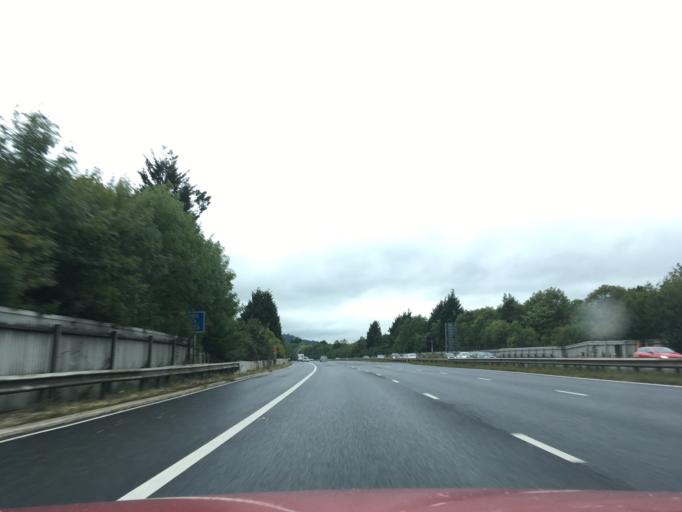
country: GB
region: England
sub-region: Gloucestershire
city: Barnwood
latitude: 51.8538
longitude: -2.1793
